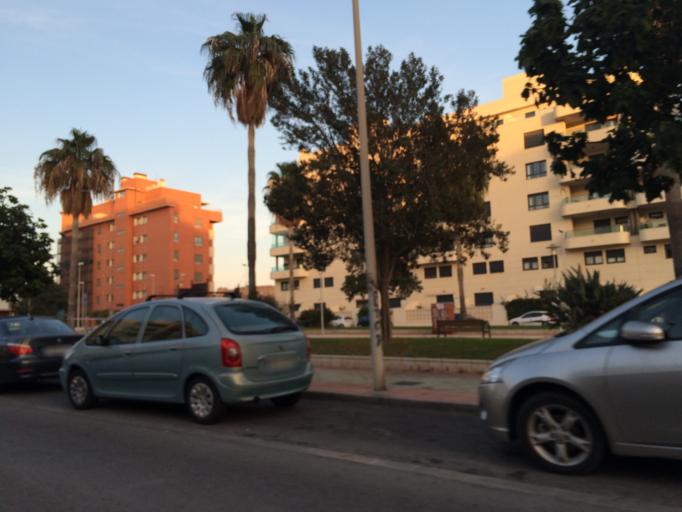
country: ES
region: Andalusia
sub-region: Provincia de Almeria
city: Almeria
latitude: 36.8234
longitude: -2.4404
